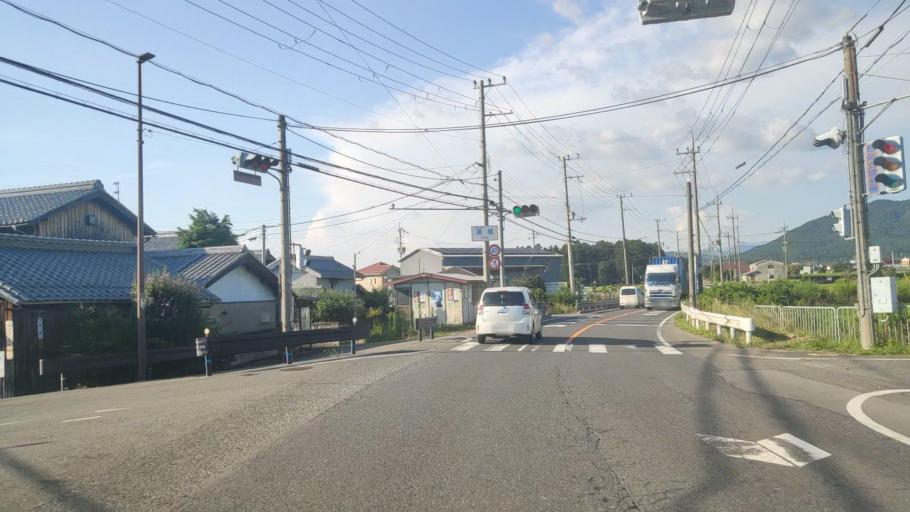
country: JP
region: Shiga Prefecture
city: Youkaichi
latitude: 35.1402
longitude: 136.2622
